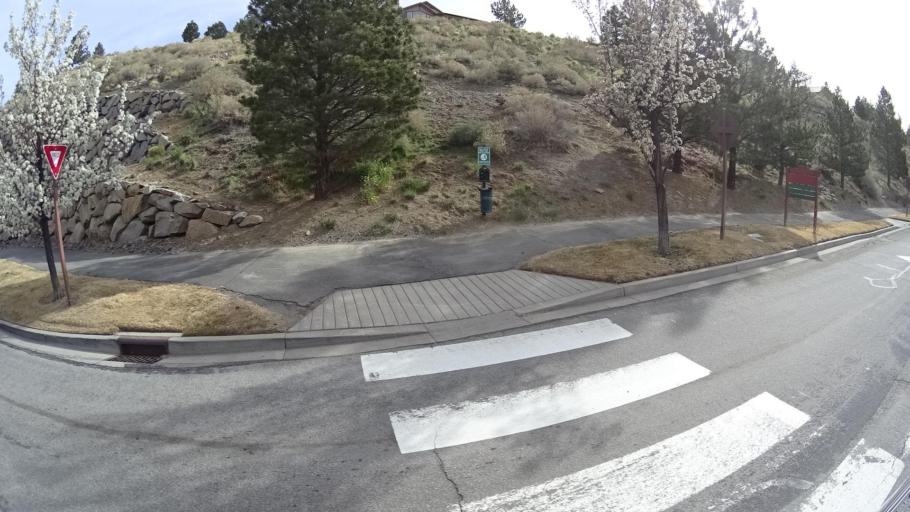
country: US
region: Nevada
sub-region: Washoe County
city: Mogul
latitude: 39.5316
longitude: -119.9108
